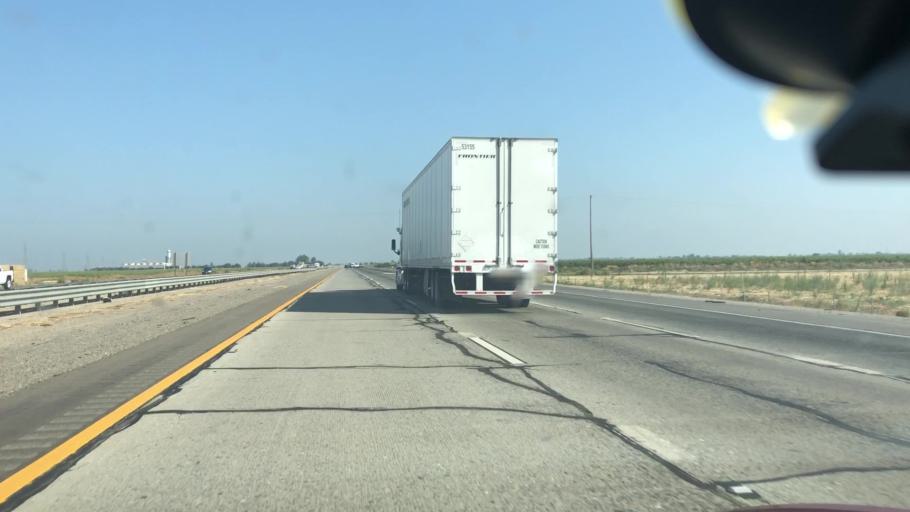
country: US
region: California
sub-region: San Joaquin County
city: Lincoln Village
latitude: 38.0709
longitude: -121.3767
